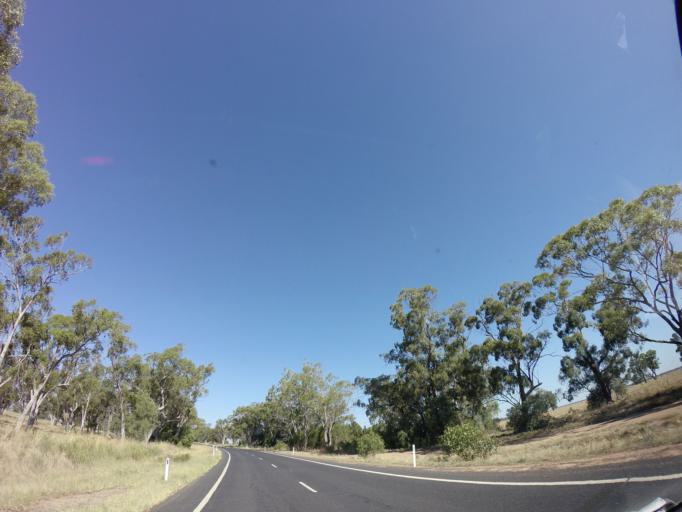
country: AU
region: New South Wales
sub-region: Narromine
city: Narromine
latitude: -31.6469
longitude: 147.9180
